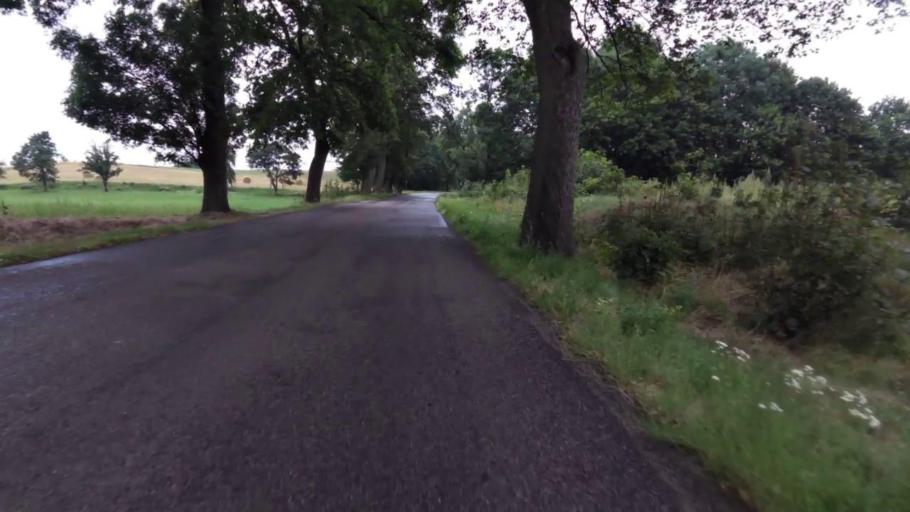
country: PL
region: West Pomeranian Voivodeship
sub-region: Powiat drawski
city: Czaplinek
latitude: 53.5877
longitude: 16.2437
